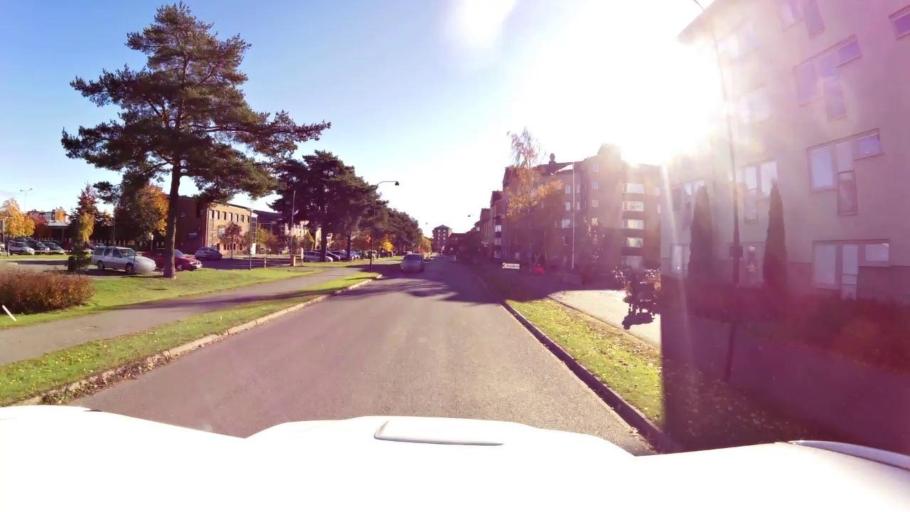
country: SE
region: OEstergoetland
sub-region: Linkopings Kommun
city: Linkoping
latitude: 58.4035
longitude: 15.6020
